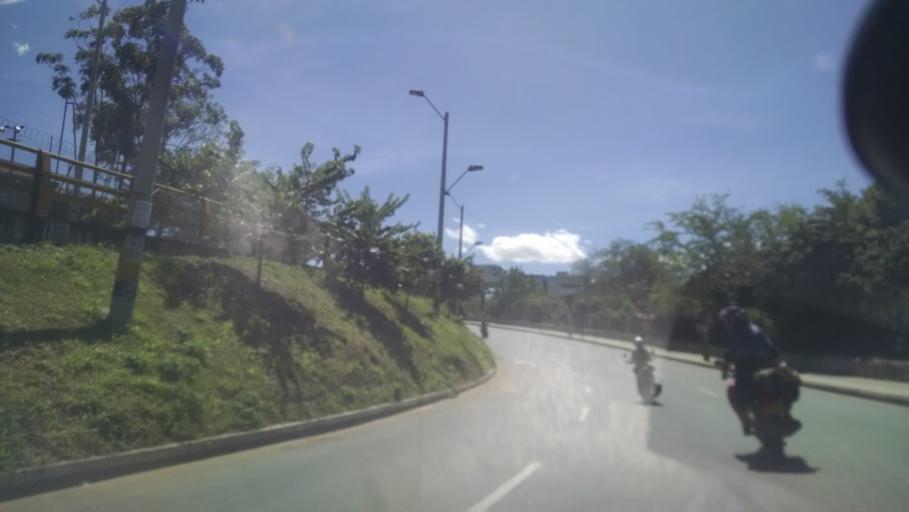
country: CO
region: Antioquia
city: Medellin
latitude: 6.2738
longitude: -75.5909
